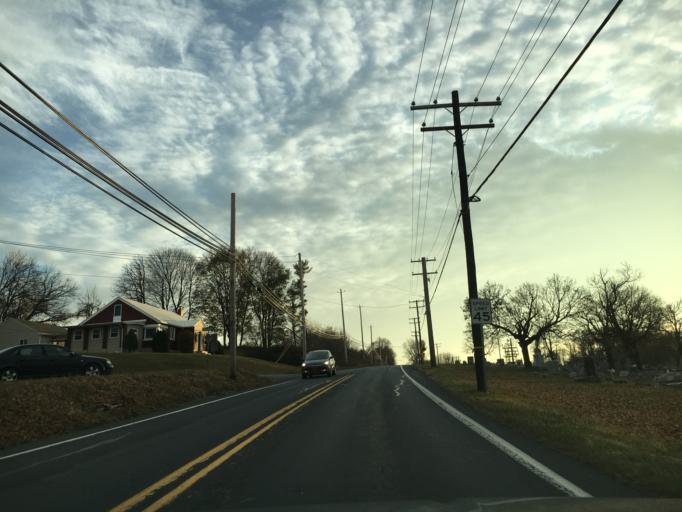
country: US
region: Pennsylvania
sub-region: Lehigh County
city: Slatington
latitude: 40.7398
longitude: -75.6124
